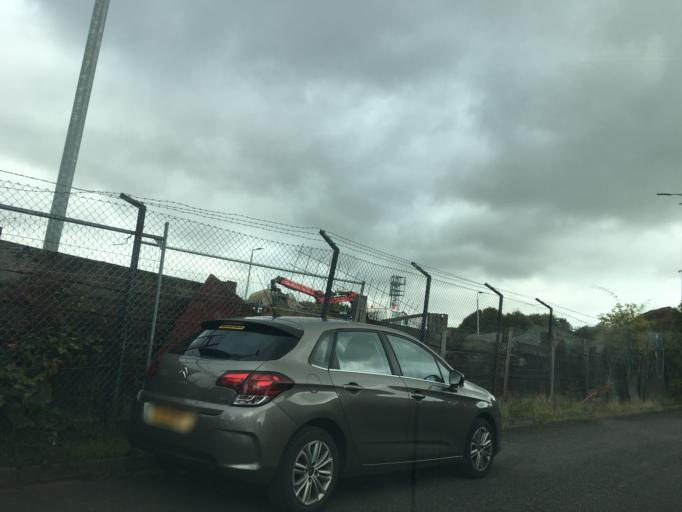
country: GB
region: Scotland
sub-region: Midlothian
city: Gorebridge
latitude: 55.8659
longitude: -3.0514
